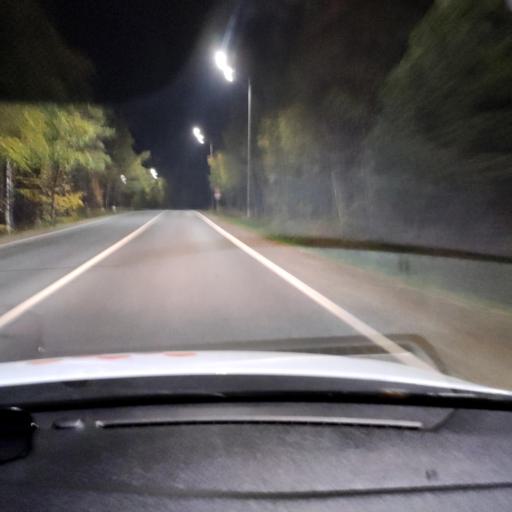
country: RU
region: Tatarstan
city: Verkhniy Uslon
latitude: 55.6356
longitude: 49.0206
